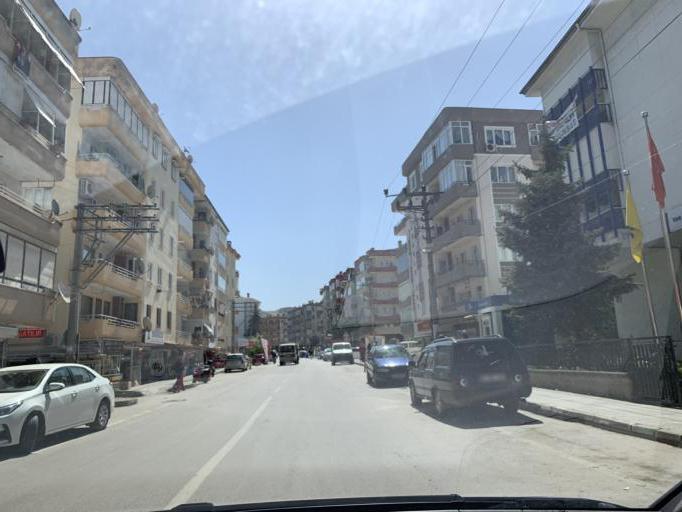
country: TR
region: Bursa
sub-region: Mudanya
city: Mudanya
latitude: 40.3550
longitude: 28.9240
